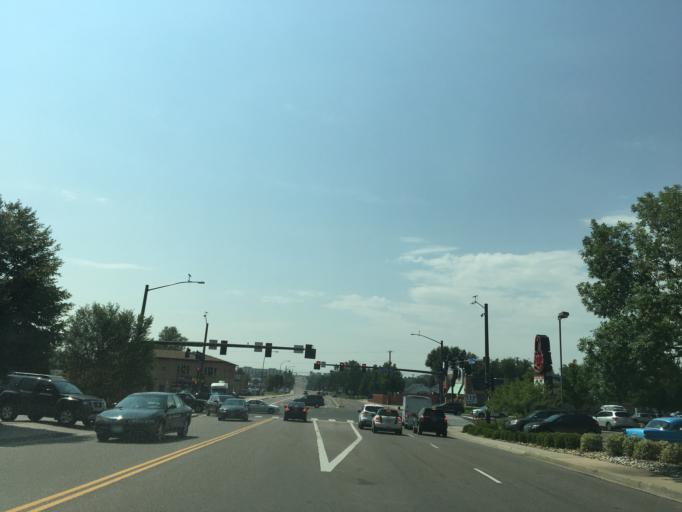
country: US
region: Colorado
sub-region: Jefferson County
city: Applewood
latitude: 39.7410
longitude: -105.1283
